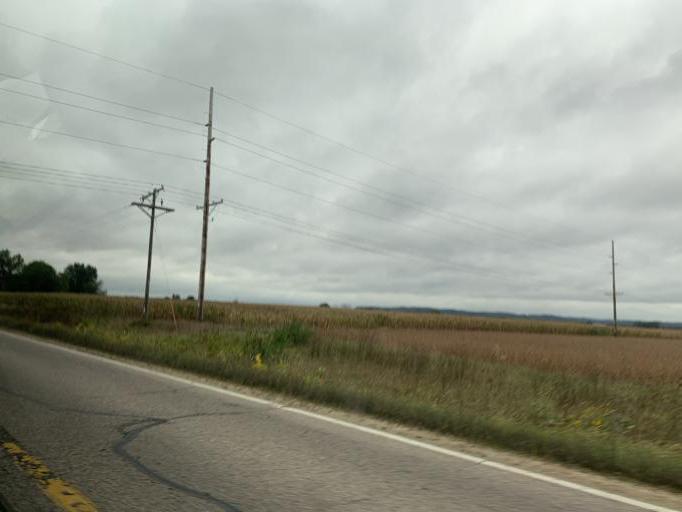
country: US
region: Wisconsin
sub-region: Sauk County
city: Spring Green
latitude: 43.1900
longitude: -90.0521
